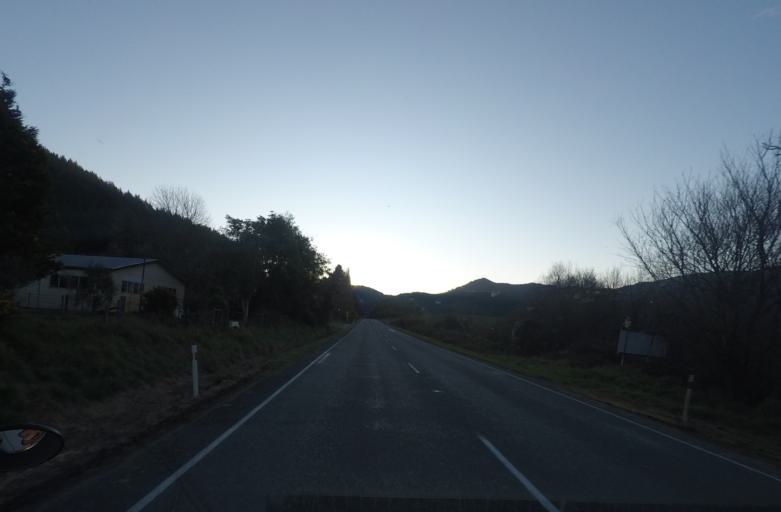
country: NZ
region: Marlborough
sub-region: Marlborough District
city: Picton
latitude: -41.2862
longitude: 173.6626
